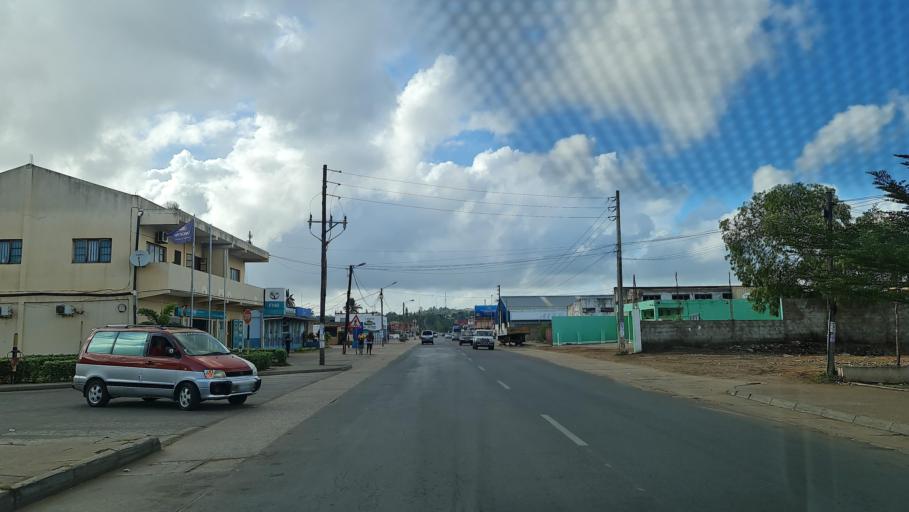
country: MZ
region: Gaza
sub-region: Xai-Xai District
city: Xai-Xai
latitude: -25.0480
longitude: 33.6454
